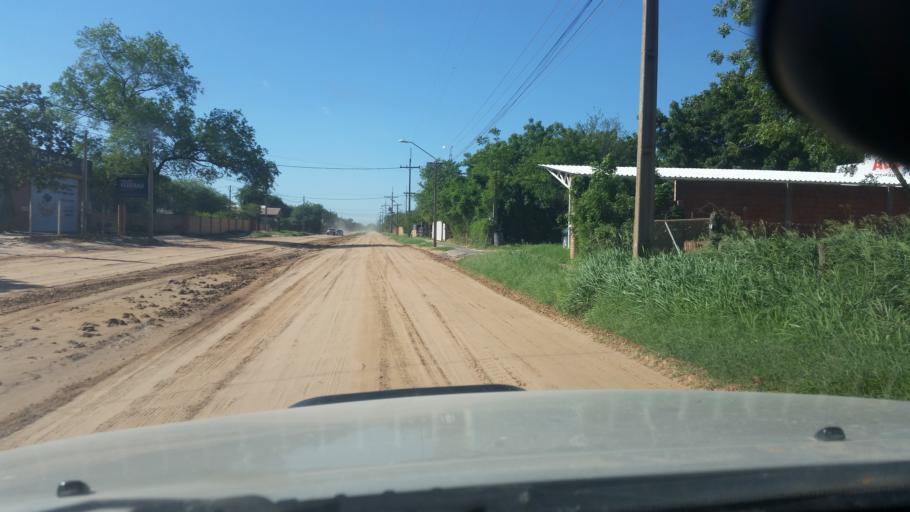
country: PY
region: Boqueron
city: Filadelfia
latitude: -22.3568
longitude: -60.0272
